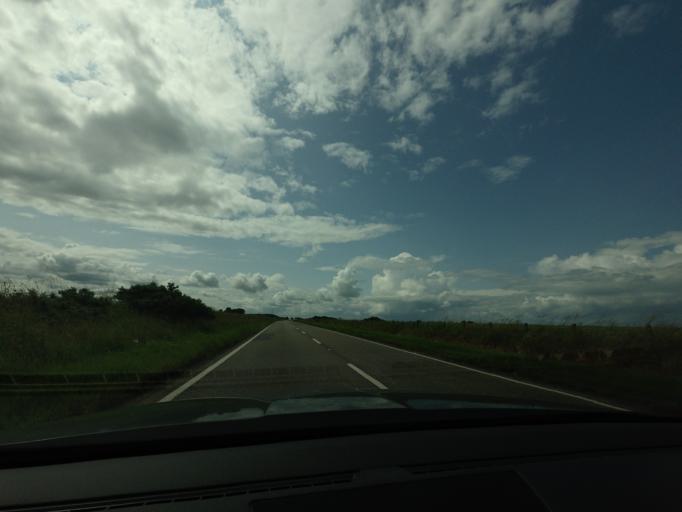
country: GB
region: Scotland
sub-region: Moray
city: Kinloss
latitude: 57.6230
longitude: -3.5439
